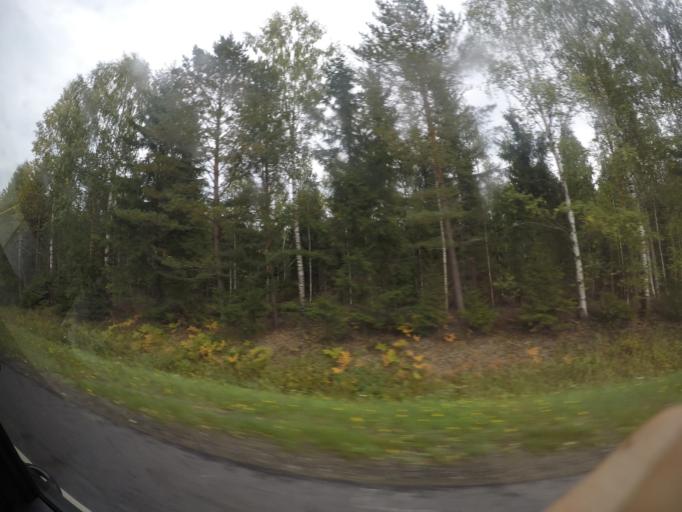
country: FI
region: Haeme
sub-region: Haemeenlinna
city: Parola
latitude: 61.1200
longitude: 24.4175
